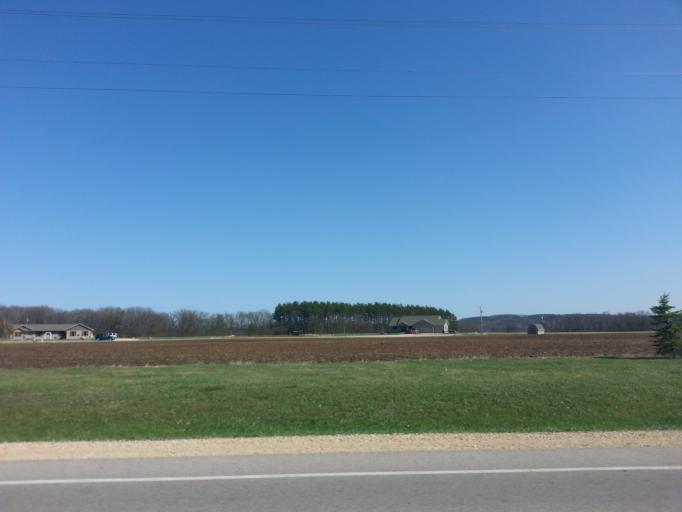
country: US
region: Wisconsin
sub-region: Pepin County
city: Durand
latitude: 44.6525
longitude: -91.9788
